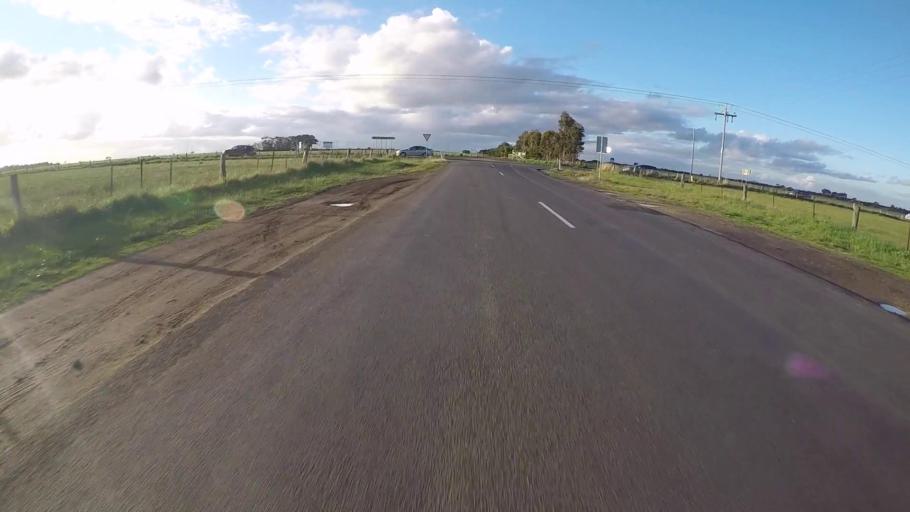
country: AU
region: Victoria
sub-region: Greater Geelong
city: Wandana Heights
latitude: -38.1223
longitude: 144.2066
